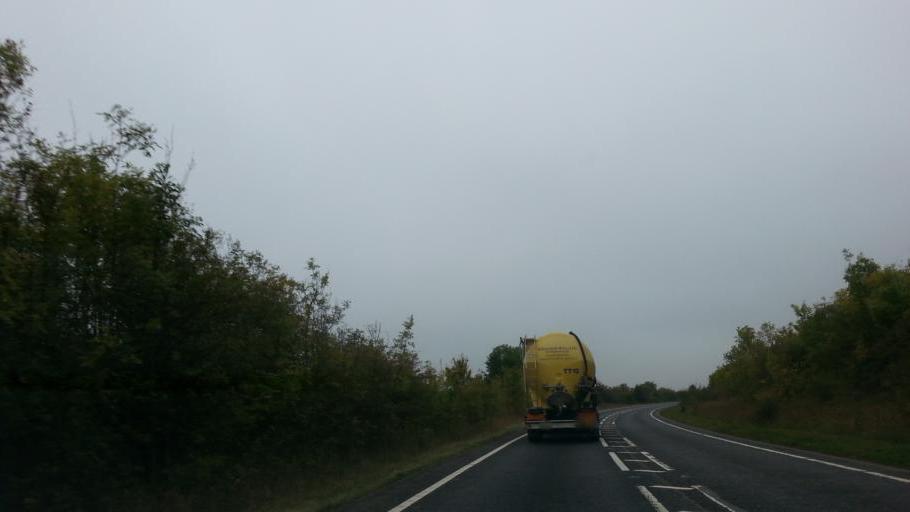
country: GB
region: England
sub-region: Northamptonshire
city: Raunds
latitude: 52.3620
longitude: -0.5310
